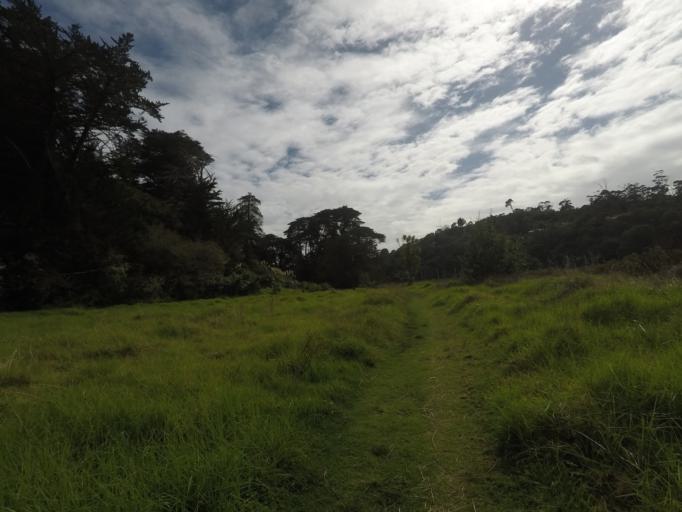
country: NZ
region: Auckland
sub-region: Auckland
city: Rothesay Bay
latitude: -36.6405
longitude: 174.7222
